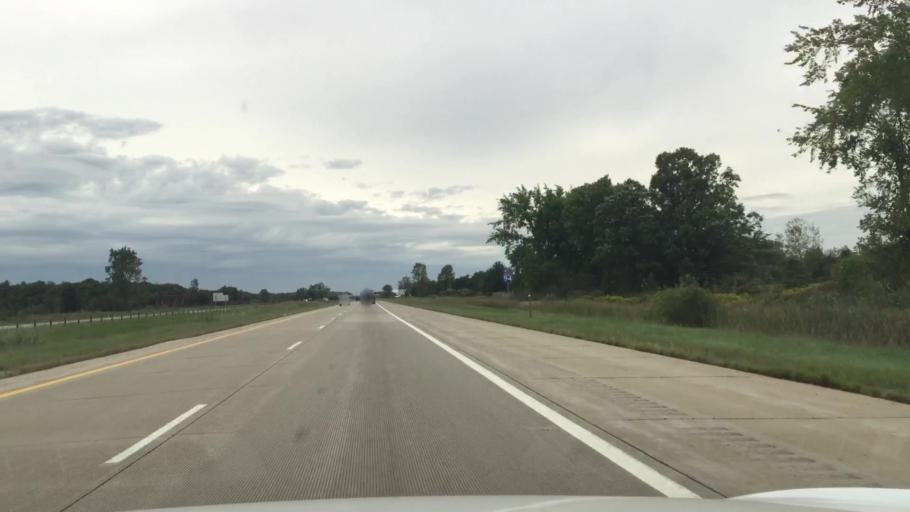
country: US
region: Michigan
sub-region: Saint Clair County
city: Saint Clair
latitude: 42.8602
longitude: -82.5609
